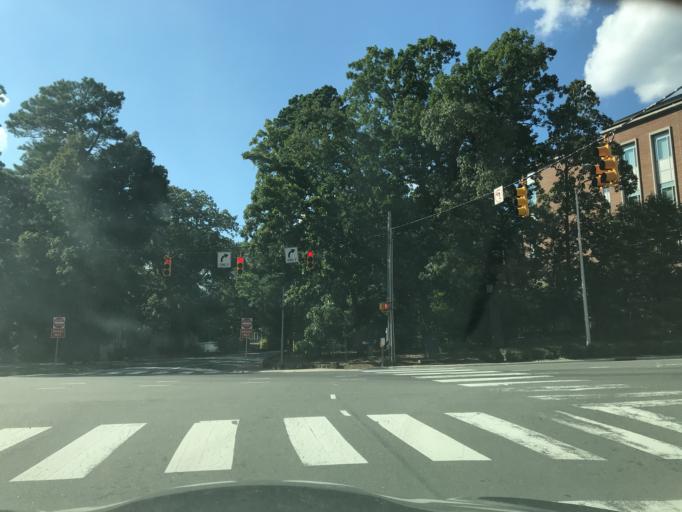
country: US
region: North Carolina
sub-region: Orange County
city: Chapel Hill
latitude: 35.9046
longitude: -79.0543
